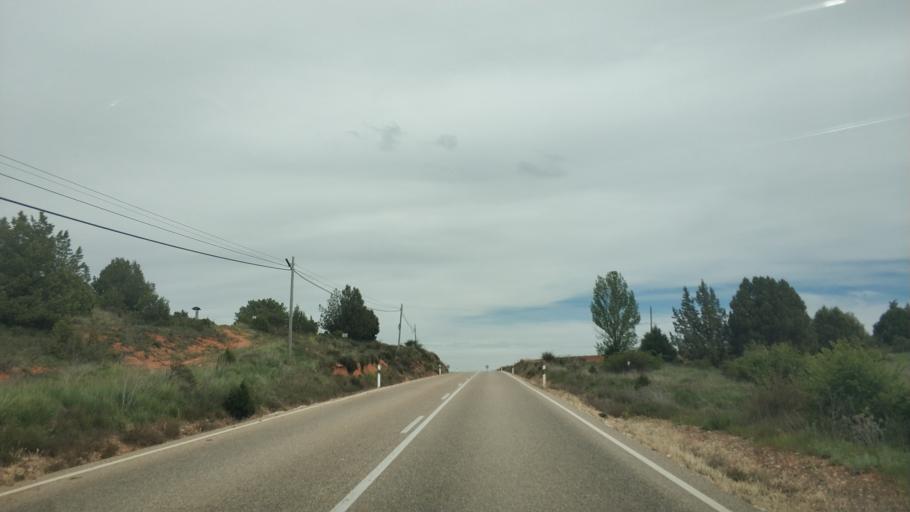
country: ES
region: Castille and Leon
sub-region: Provincia de Soria
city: El Burgo de Osma
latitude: 41.5764
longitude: -3.0277
